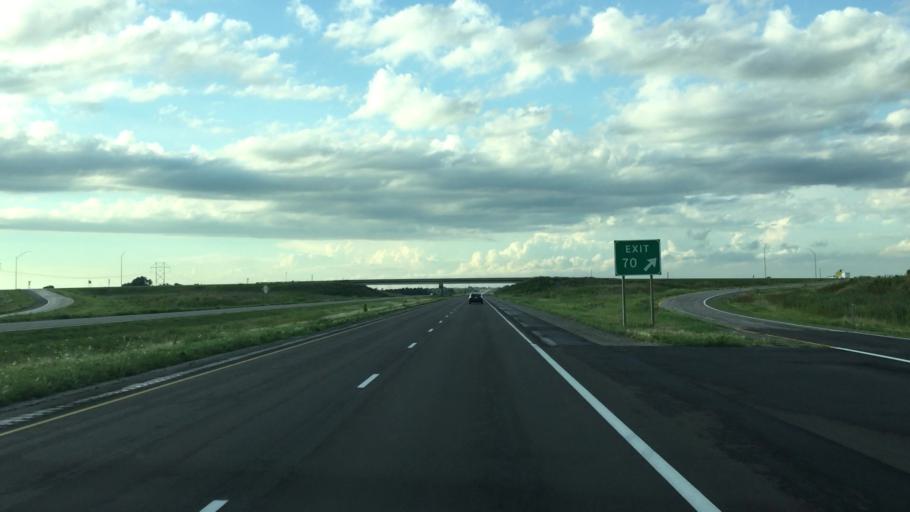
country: US
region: Iowa
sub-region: Washington County
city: Washington
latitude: 41.3335
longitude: -91.5518
